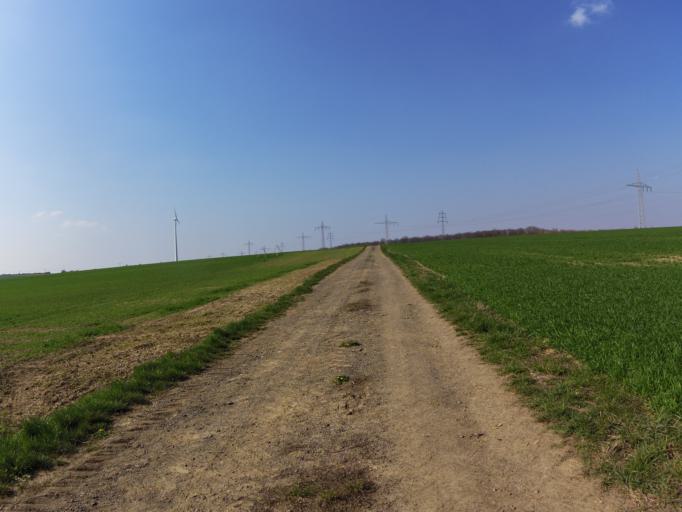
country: DE
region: Bavaria
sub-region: Regierungsbezirk Unterfranken
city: Theilheim
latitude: 49.7681
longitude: 10.0438
